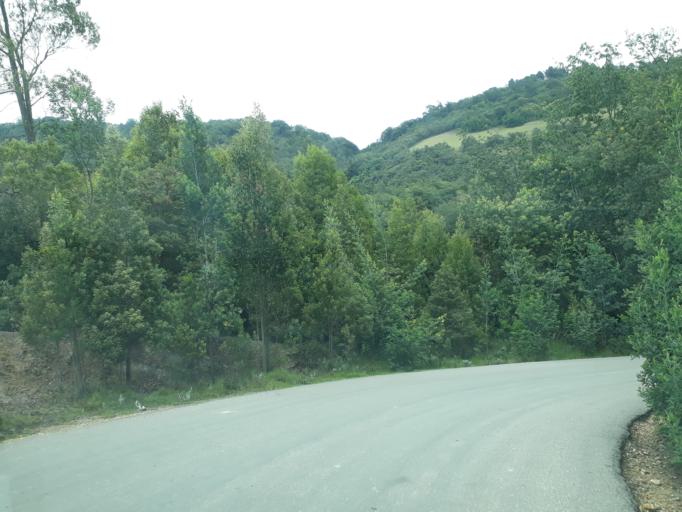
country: CO
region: Cundinamarca
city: Cucunuba
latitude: 5.2092
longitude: -73.7875
